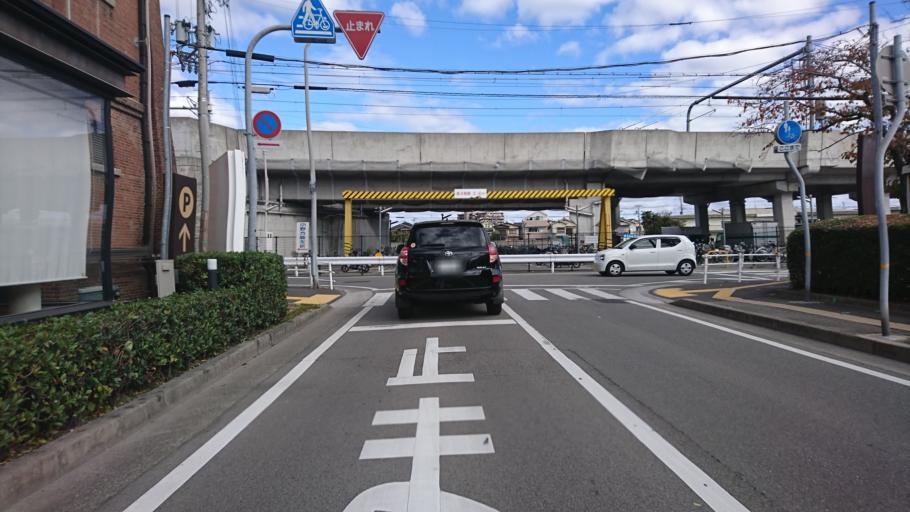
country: JP
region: Hyogo
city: Kakogawacho-honmachi
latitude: 34.7707
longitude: 134.8357
